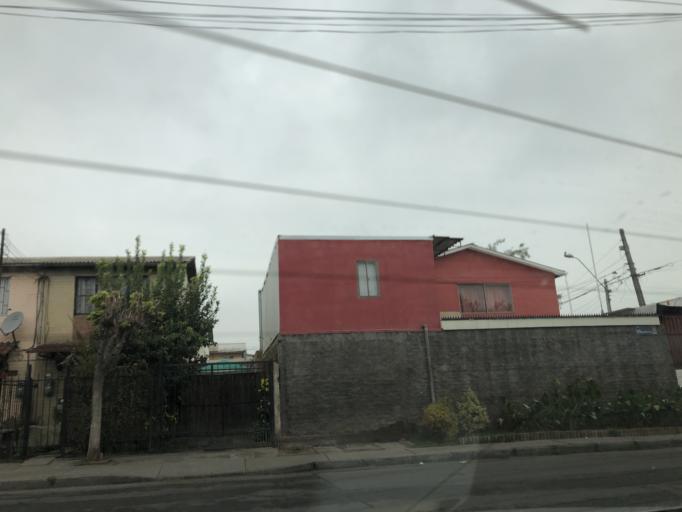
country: CL
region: Santiago Metropolitan
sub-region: Provincia de Cordillera
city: Puente Alto
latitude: -33.5850
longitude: -70.5947
